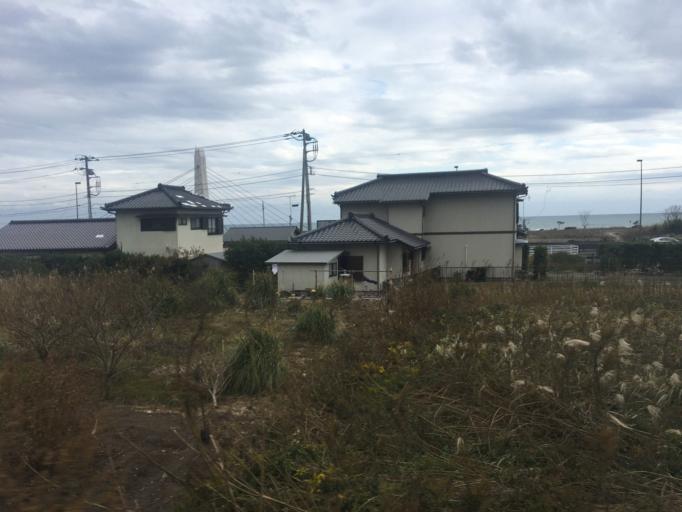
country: JP
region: Chiba
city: Kawaguchi
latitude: 35.0300
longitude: 139.9972
